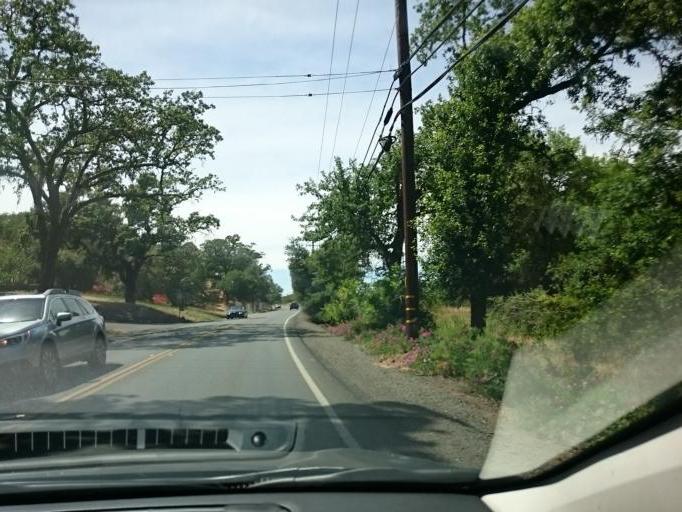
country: US
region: California
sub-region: Sonoma County
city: Healdsburg
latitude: 38.6599
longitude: -122.8407
